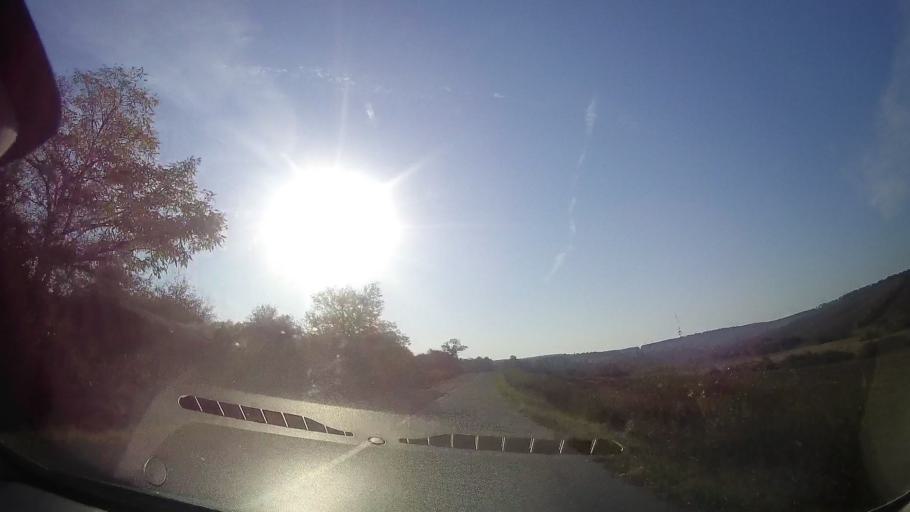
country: RO
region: Timis
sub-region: Comuna Bogda
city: Bogda
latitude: 45.9672
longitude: 21.6083
